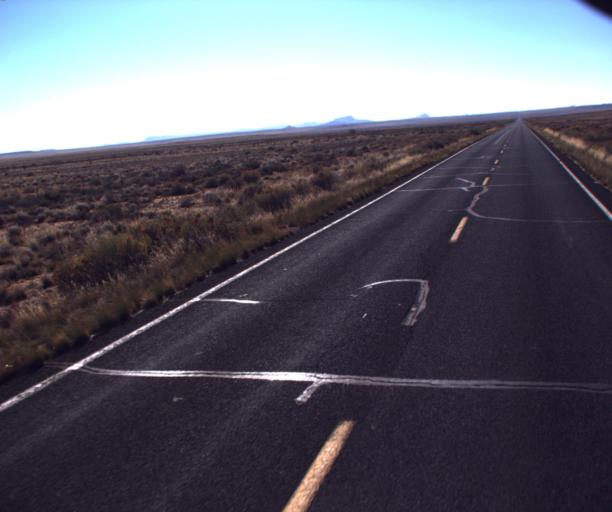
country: US
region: Arizona
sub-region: Navajo County
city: First Mesa
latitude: 35.7137
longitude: -110.5124
